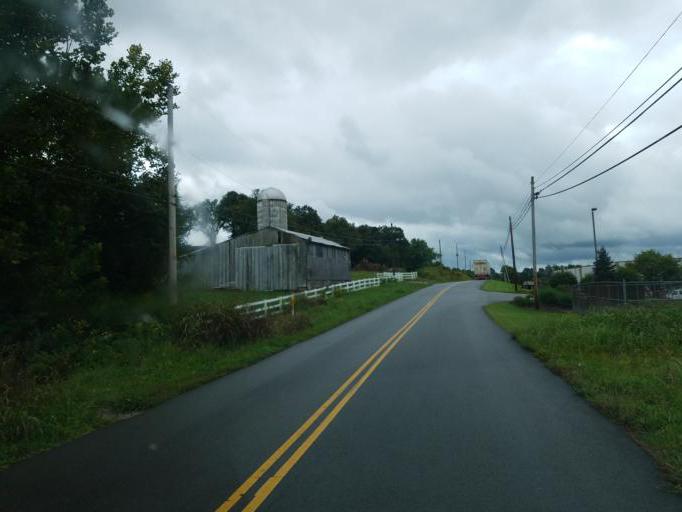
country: US
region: Ohio
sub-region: Scioto County
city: Franklin Furnace
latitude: 38.6822
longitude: -82.8561
